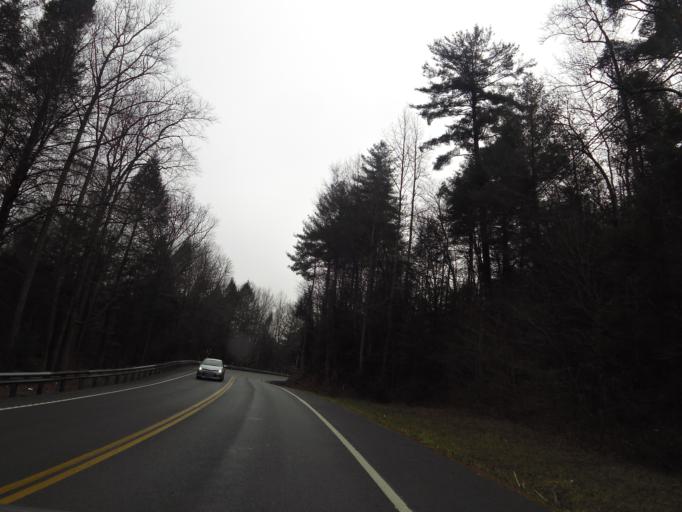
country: US
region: Tennessee
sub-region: Morgan County
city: Wartburg
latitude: 36.0424
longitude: -84.5272
